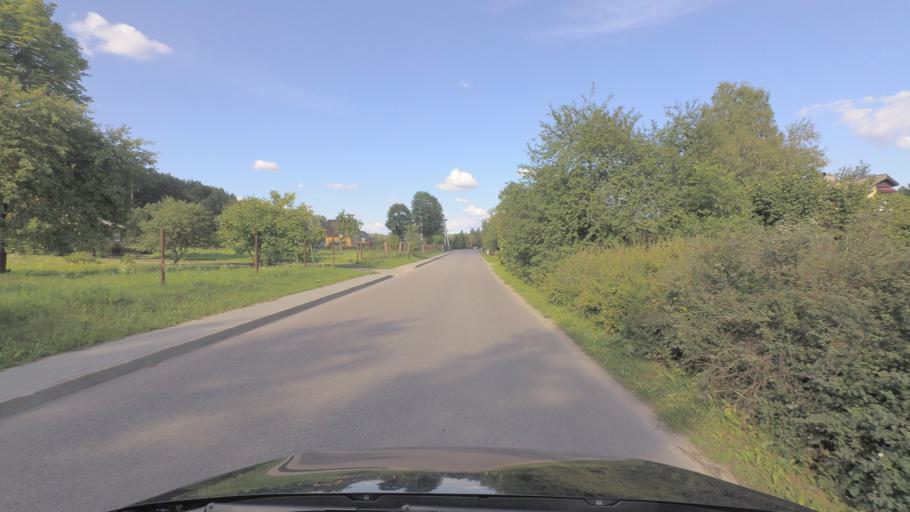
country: LT
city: Nemencine
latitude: 54.8542
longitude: 25.3781
